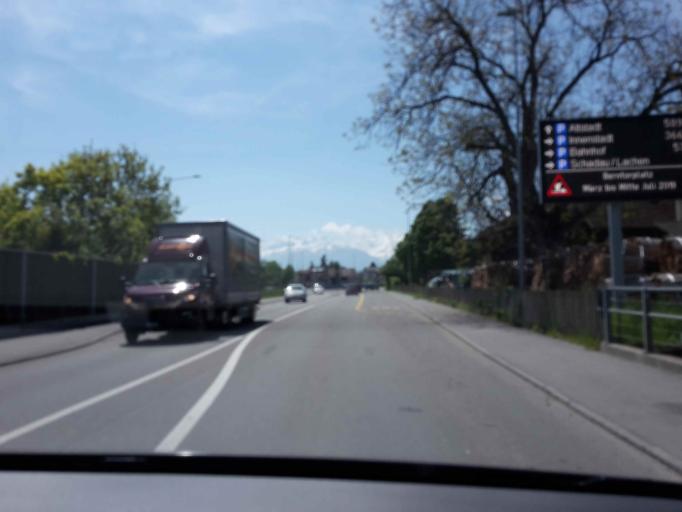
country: CH
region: Bern
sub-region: Thun District
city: Steffisburg
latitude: 46.7715
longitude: 7.6181
